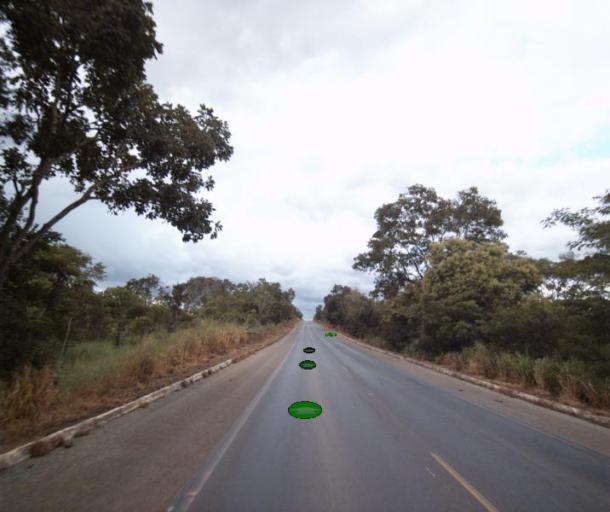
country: BR
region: Goias
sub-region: Uruacu
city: Uruacu
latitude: -14.7764
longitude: -49.2696
